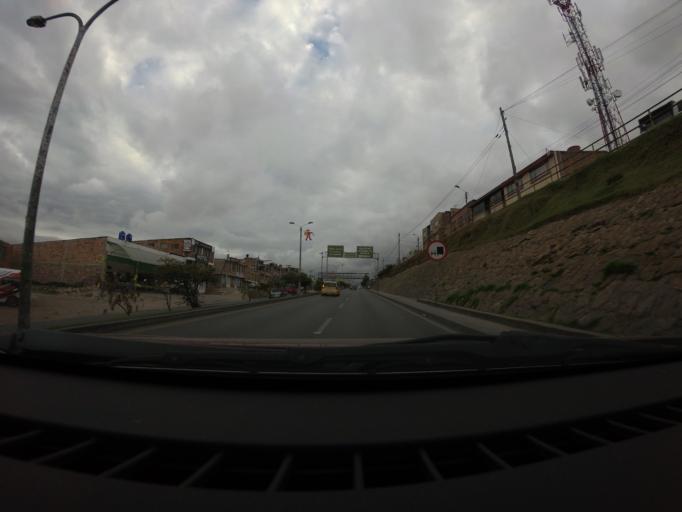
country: CO
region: Boyaca
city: Tunja
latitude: 5.5242
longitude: -73.3623
